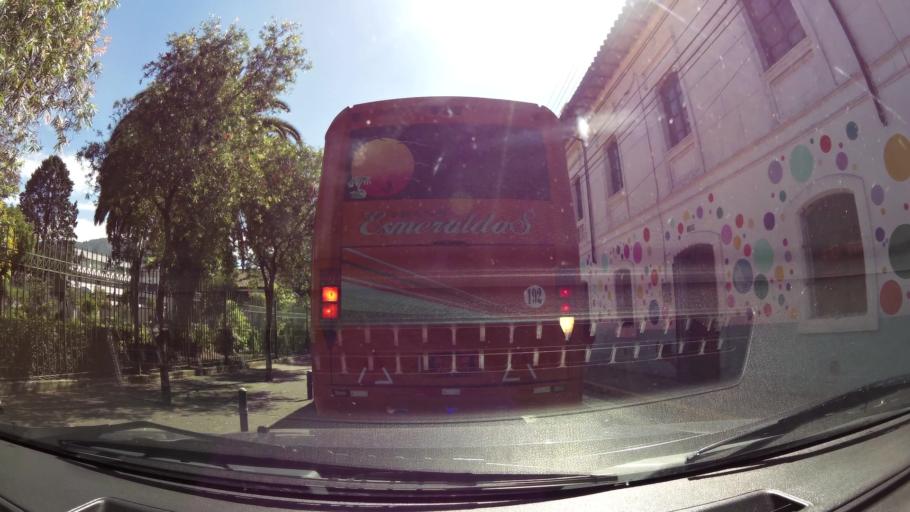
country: EC
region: Pichincha
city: Quito
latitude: -0.2761
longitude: -78.5538
